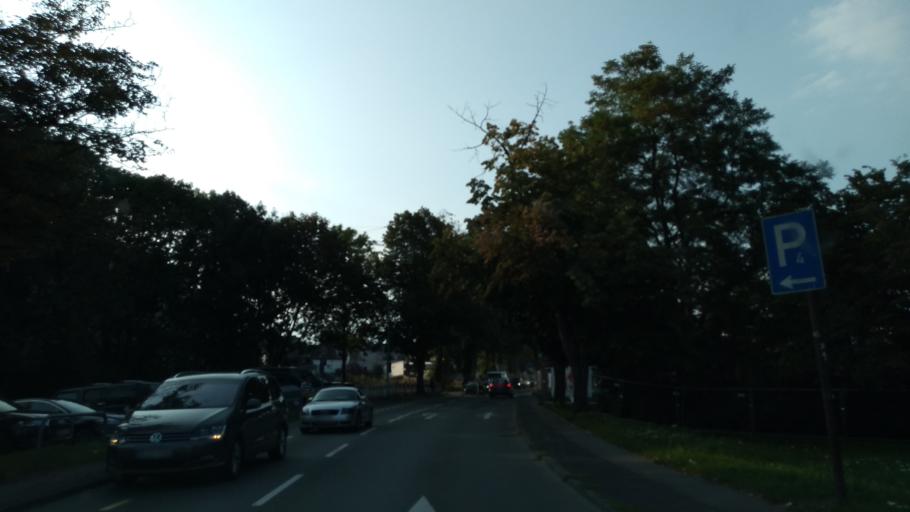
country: DE
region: North Rhine-Westphalia
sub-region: Regierungsbezirk Koln
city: Siegburg
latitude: 50.7983
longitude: 7.2139
